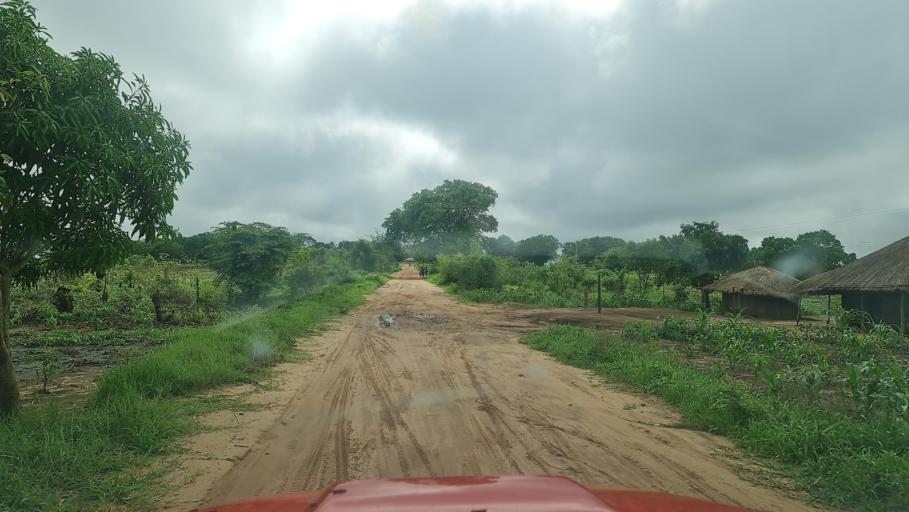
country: MW
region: Southern Region
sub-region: Nsanje District
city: Nsanje
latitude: -17.2031
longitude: 35.6928
